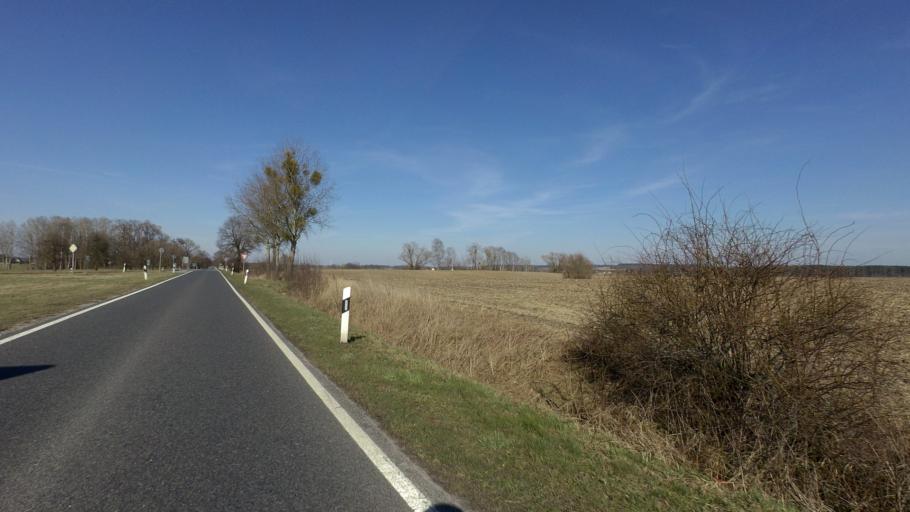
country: DE
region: Brandenburg
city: Angermunde
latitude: 52.9703
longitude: 13.9656
